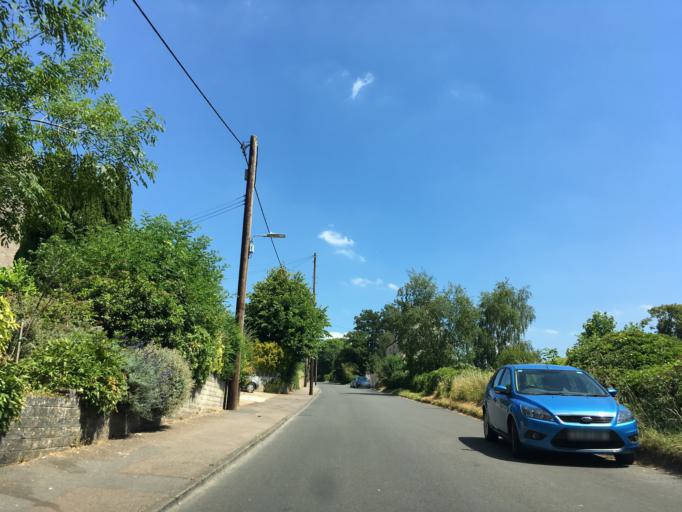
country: GB
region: England
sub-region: Gloucestershire
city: Stroud
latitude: 51.7424
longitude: -2.1977
